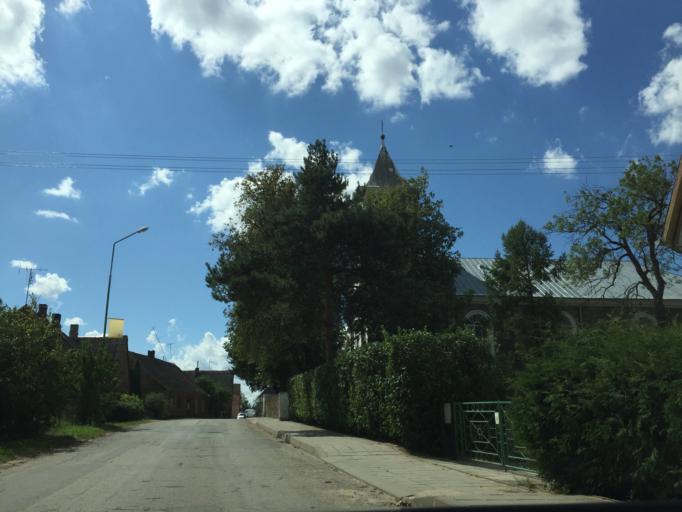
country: LV
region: Rundales
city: Pilsrundale
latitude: 56.2739
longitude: 23.9999
